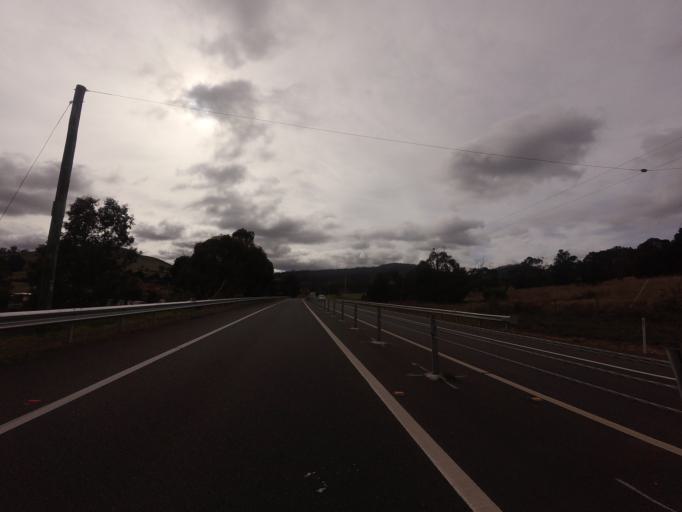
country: AU
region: Tasmania
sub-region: Brighton
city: Bridgewater
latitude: -42.5959
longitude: 147.2212
